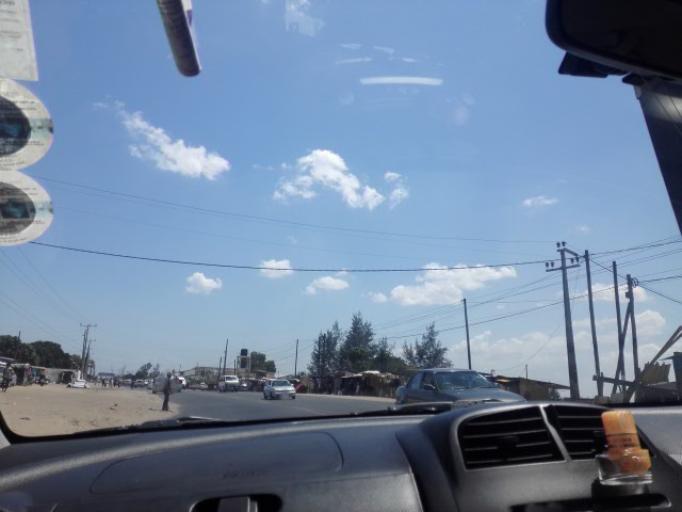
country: MZ
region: Maputo City
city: Maputo
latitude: -25.8543
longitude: 32.5675
